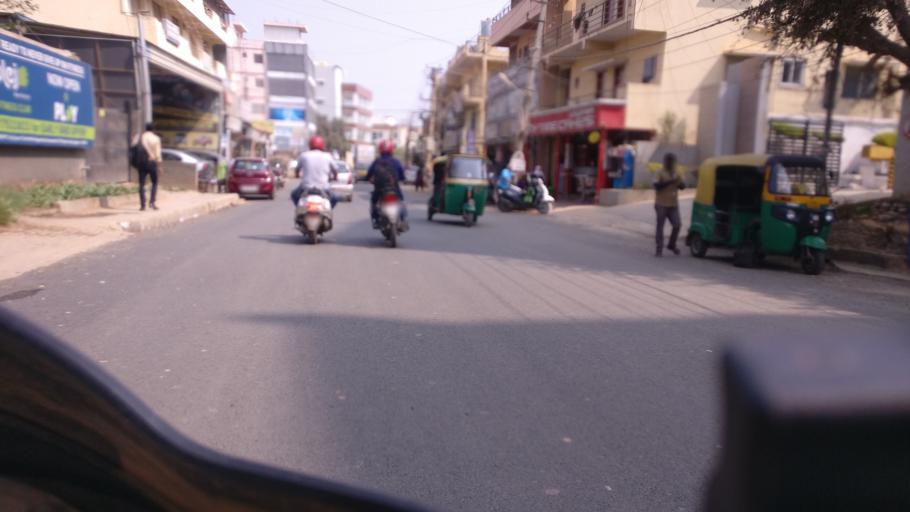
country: IN
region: Karnataka
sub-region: Bangalore Urban
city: Bangalore
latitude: 12.9115
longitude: 77.6766
